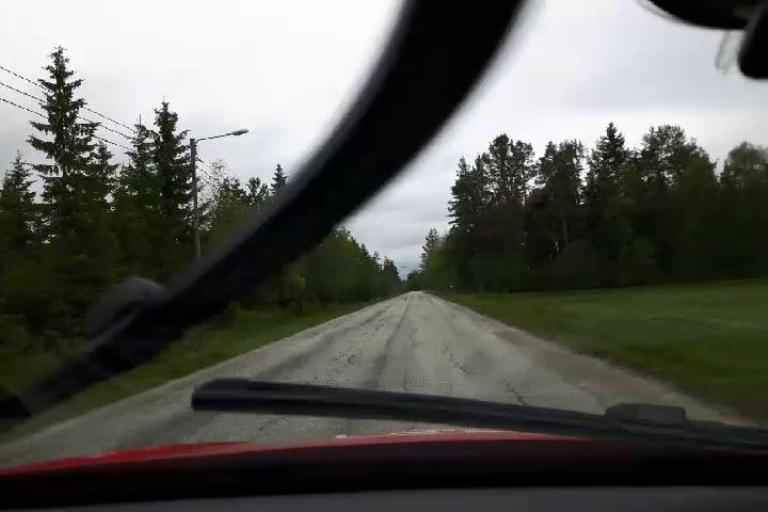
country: SE
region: Jaemtland
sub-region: Bergs Kommun
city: Hoverberg
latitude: 62.7410
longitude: 14.4232
